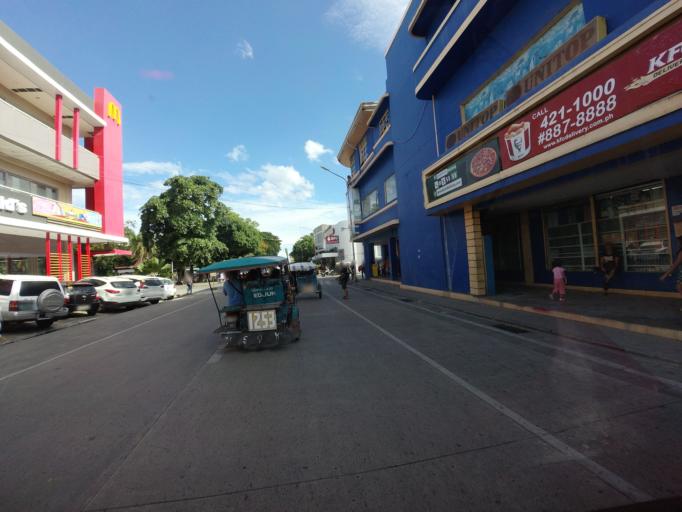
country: PH
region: Central Visayas
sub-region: Province of Negros Oriental
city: Dumaguete
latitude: 9.3068
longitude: 123.3076
